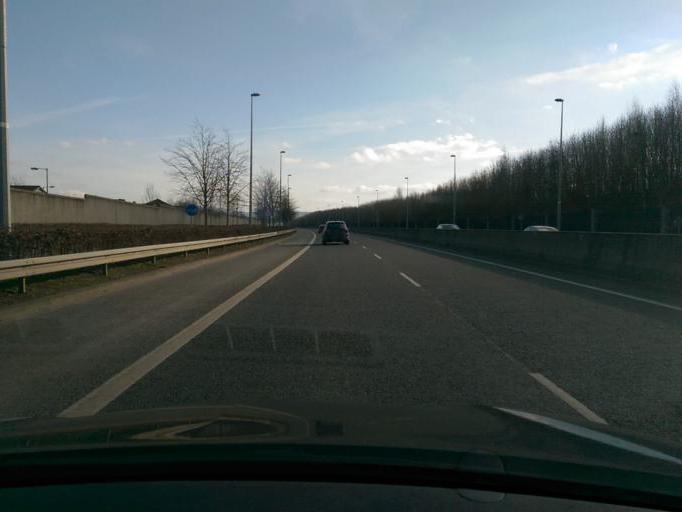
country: IE
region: Leinster
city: Clondalkin
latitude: 53.3262
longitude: -6.4321
